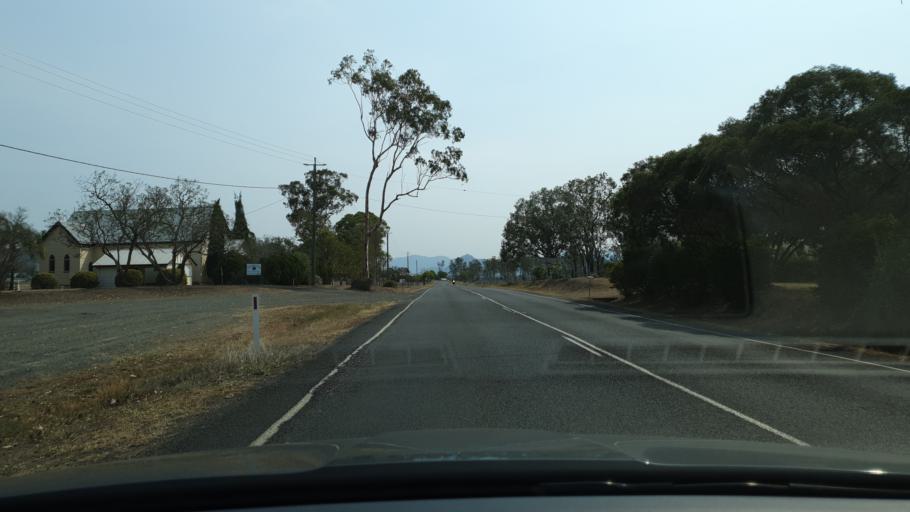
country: AU
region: Queensland
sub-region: Ipswich
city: Deebing Heights
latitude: -28.0129
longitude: 152.6760
